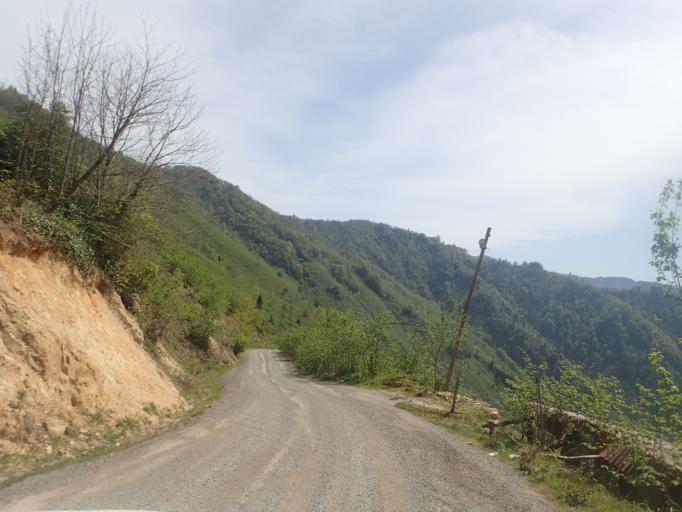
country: TR
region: Ordu
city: Kabaduz
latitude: 40.7975
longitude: 37.9074
